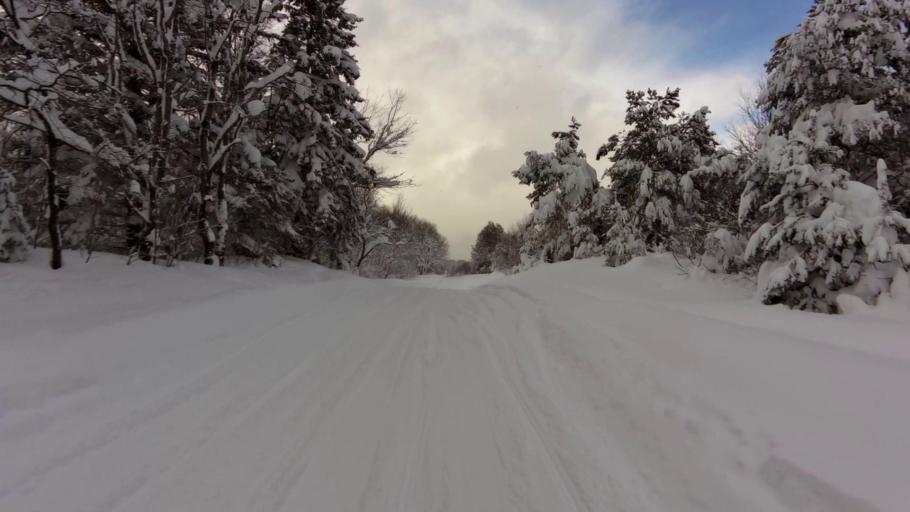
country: US
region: New York
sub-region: Lewis County
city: Lowville
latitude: 43.7383
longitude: -75.6719
